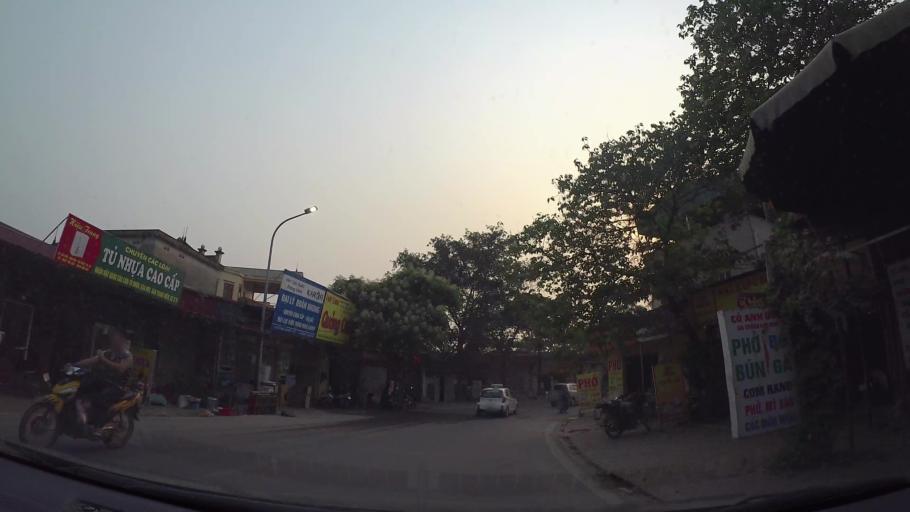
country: VN
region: Ha Noi
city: Thuong Tin
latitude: 20.8687
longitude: 105.8302
